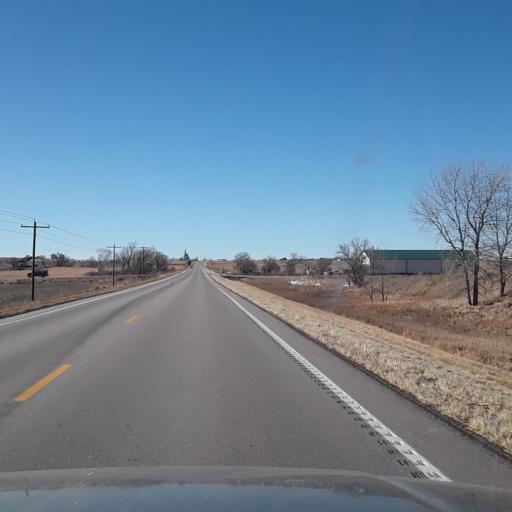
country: US
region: Nebraska
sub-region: Dawson County
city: Gothenburg
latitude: 40.7039
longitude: -100.1825
